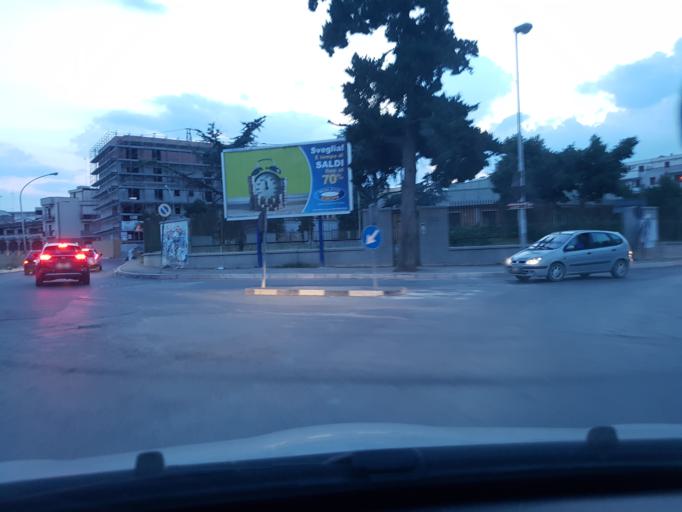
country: IT
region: Apulia
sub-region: Provincia di Foggia
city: Cerignola
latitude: 41.2624
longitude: 15.8885
